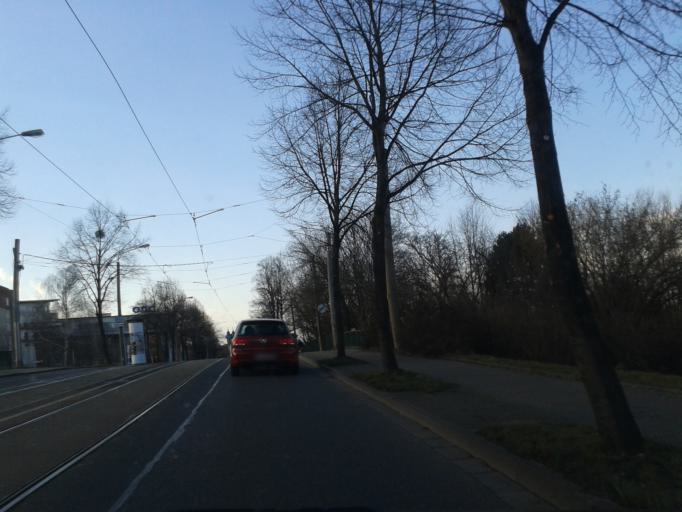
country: DE
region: Saxony
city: Dresden
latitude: 51.0180
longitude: 13.7833
